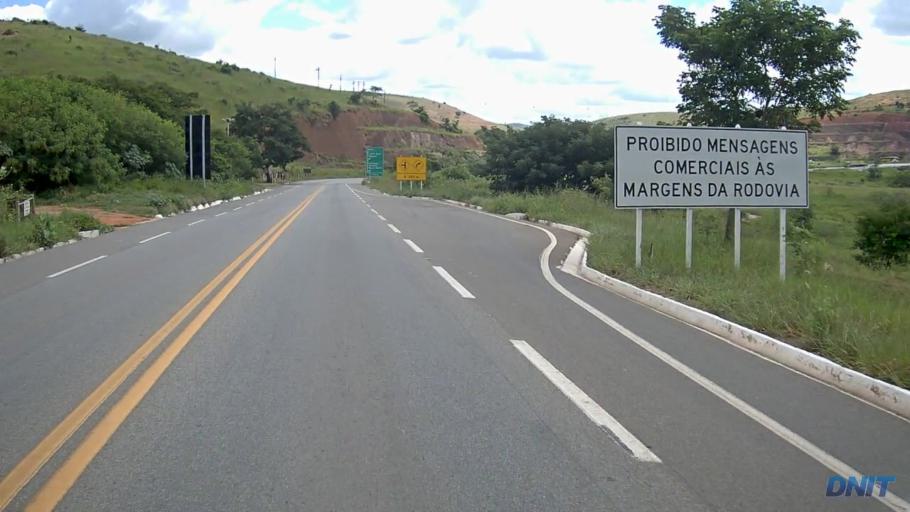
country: BR
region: Minas Gerais
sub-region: Governador Valadares
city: Governador Valadares
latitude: -18.8629
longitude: -41.9873
